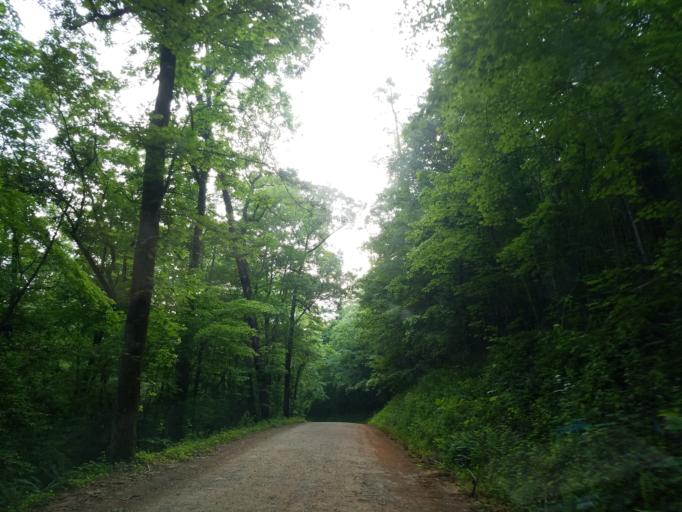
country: US
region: Georgia
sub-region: Lumpkin County
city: Dahlonega
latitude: 34.6033
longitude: -84.0999
